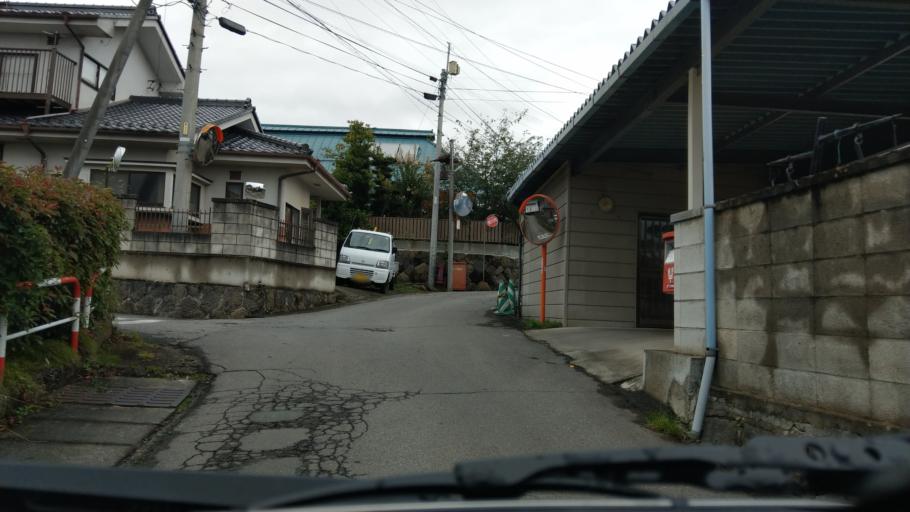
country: JP
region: Nagano
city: Komoro
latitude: 36.3519
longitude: 138.4313
